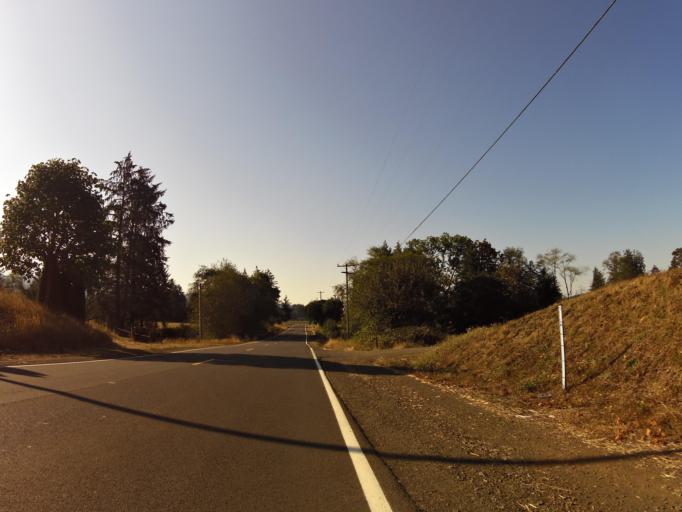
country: US
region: Oregon
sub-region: Tillamook County
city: Tillamook
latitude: 45.3969
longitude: -123.7931
